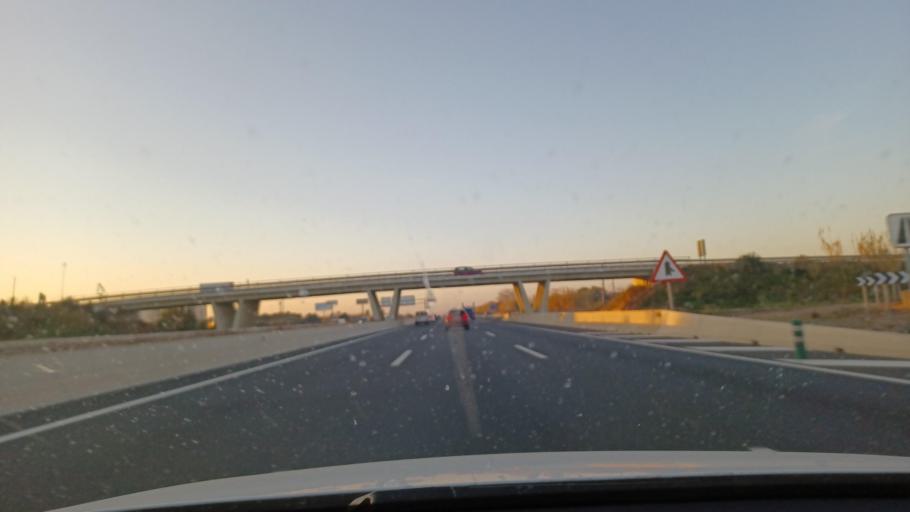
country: ES
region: Valencia
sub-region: Provincia de Valencia
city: Puig
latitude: 39.5692
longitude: -0.2958
